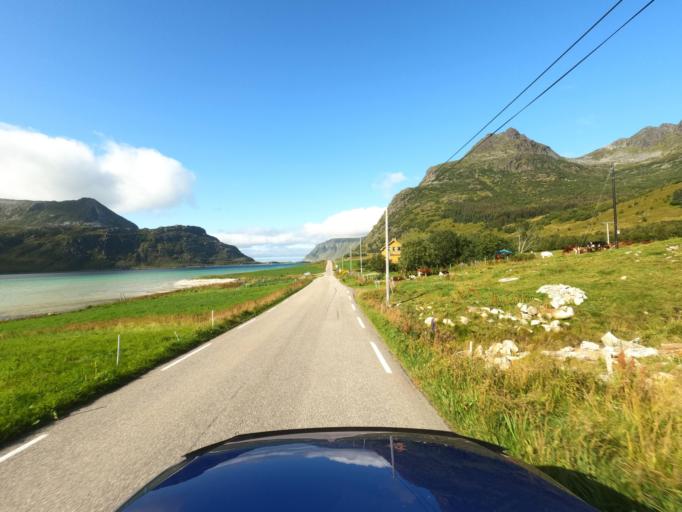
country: NO
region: Nordland
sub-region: Flakstad
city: Ramberg
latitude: 68.0823
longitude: 13.3429
